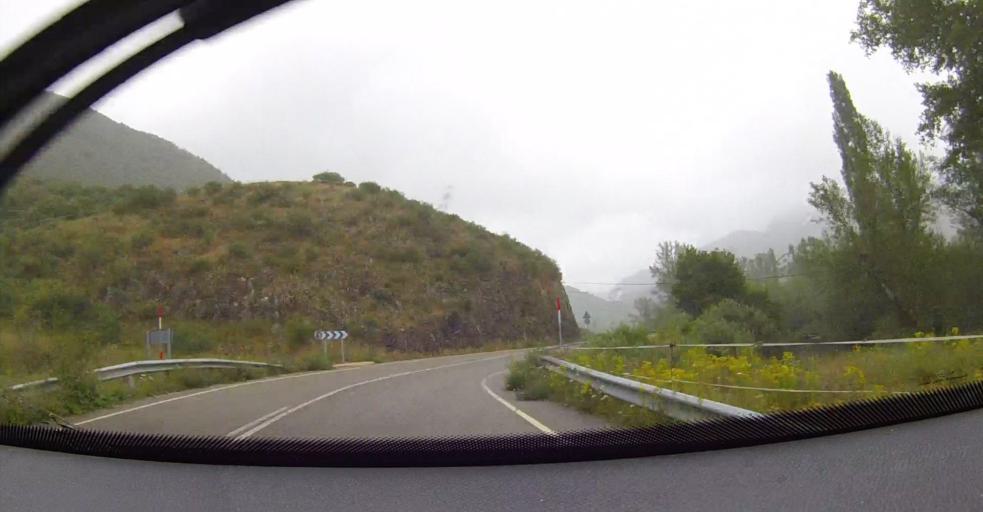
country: ES
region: Castille and Leon
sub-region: Provincia de Leon
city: Acebedo
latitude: 43.0426
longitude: -5.1112
